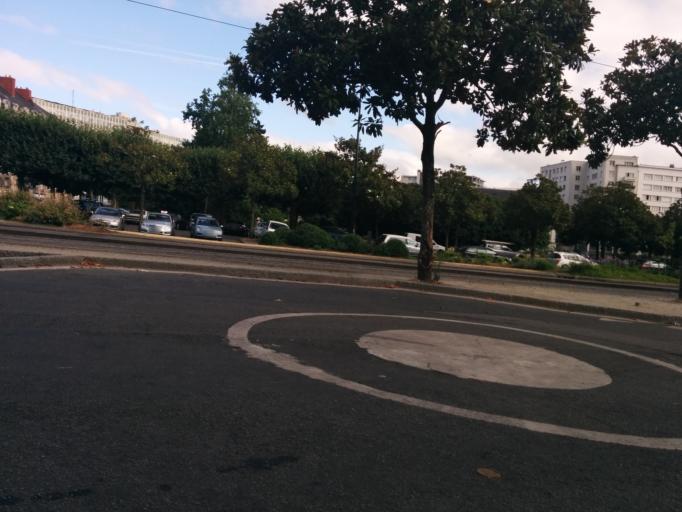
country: FR
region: Pays de la Loire
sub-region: Departement de la Loire-Atlantique
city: Nantes
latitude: 47.2126
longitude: -1.5584
